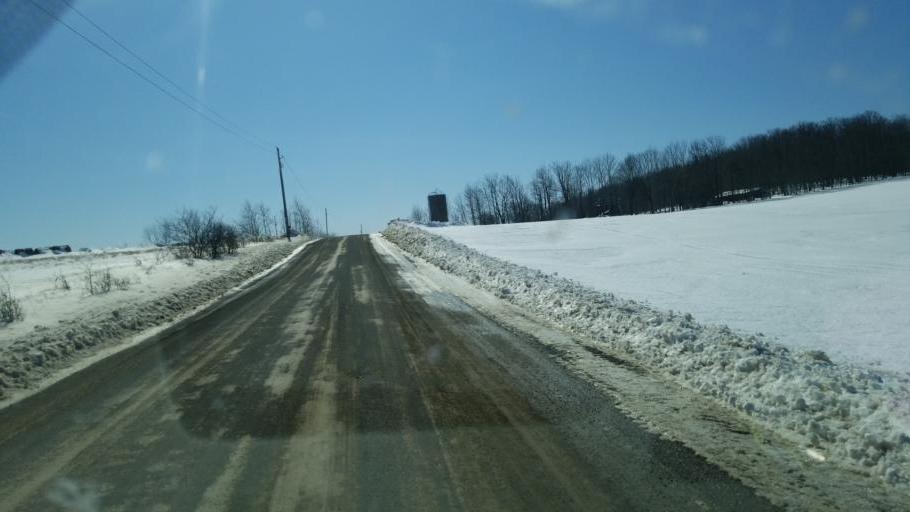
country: US
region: New York
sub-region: Allegany County
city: Alfred
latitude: 42.2666
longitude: -77.7323
